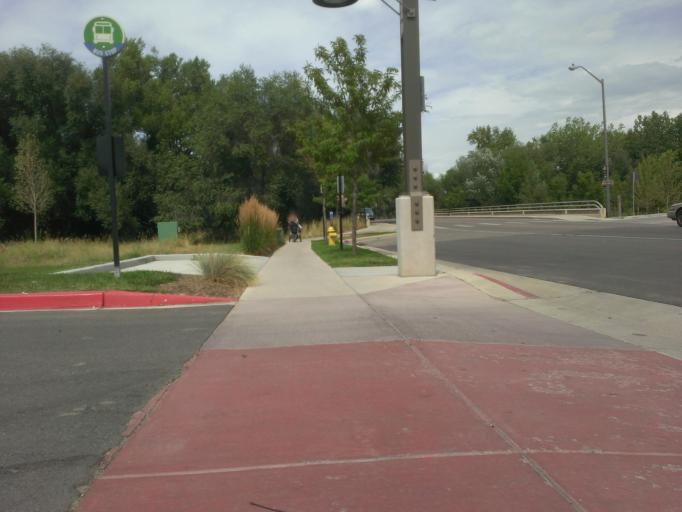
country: US
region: Colorado
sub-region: Larimer County
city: Fort Collins
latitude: 40.5909
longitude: -105.0722
